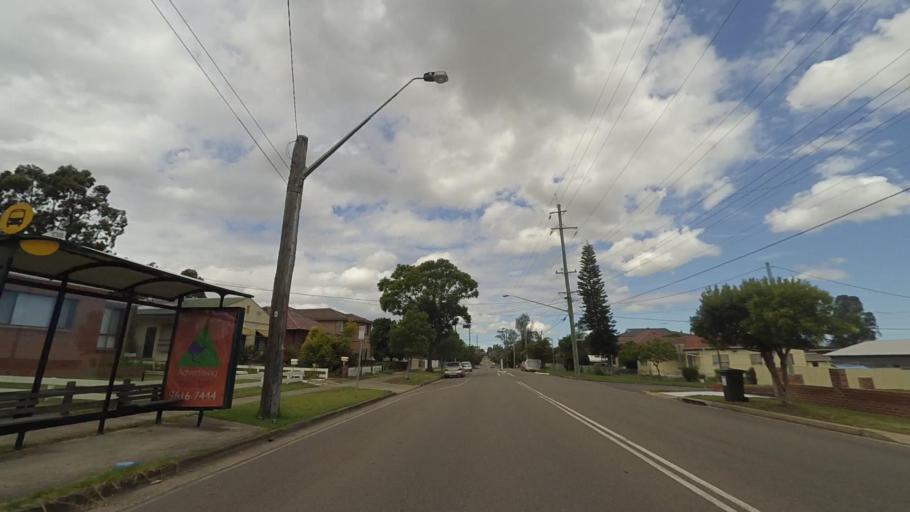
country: AU
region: New South Wales
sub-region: Holroyd
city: Guildford West
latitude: -33.8506
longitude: 150.9621
